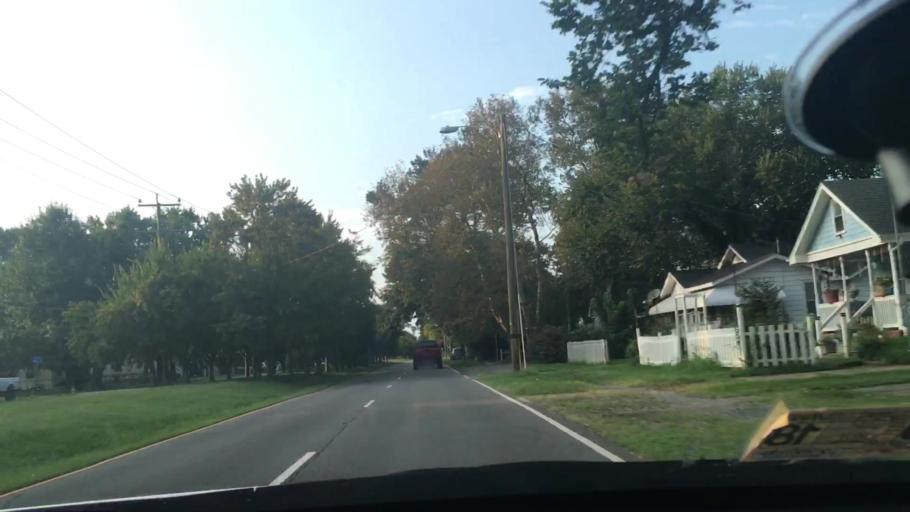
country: US
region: Virginia
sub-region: City of Norfolk
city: Norfolk
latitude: 36.9350
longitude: -76.2446
